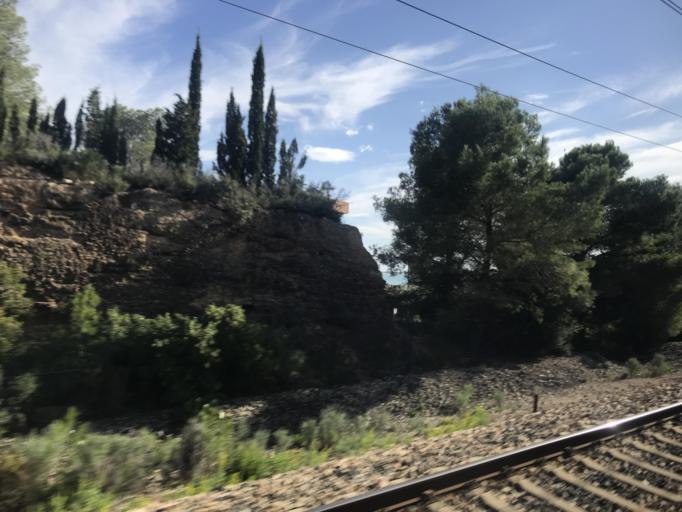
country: ES
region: Catalonia
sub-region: Provincia de Tarragona
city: L'Ampolla
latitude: 40.8287
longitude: 0.7358
